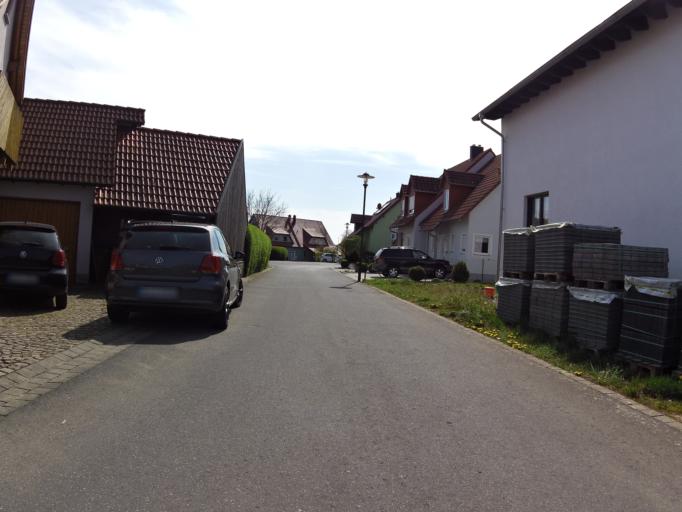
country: DE
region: Bavaria
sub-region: Regierungsbezirk Unterfranken
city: Unterpleichfeld
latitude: 49.8710
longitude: 10.0399
